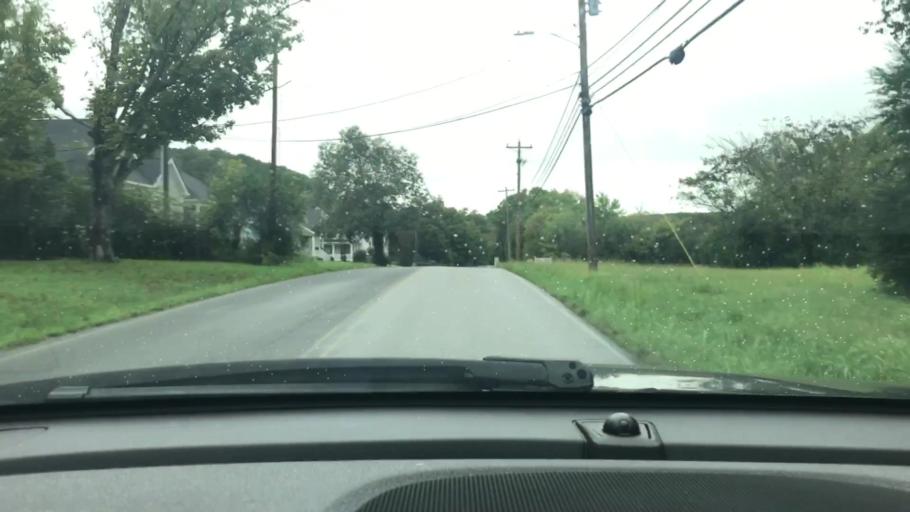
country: US
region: Tennessee
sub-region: Cheatham County
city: Kingston Springs
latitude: 36.1017
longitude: -87.1173
